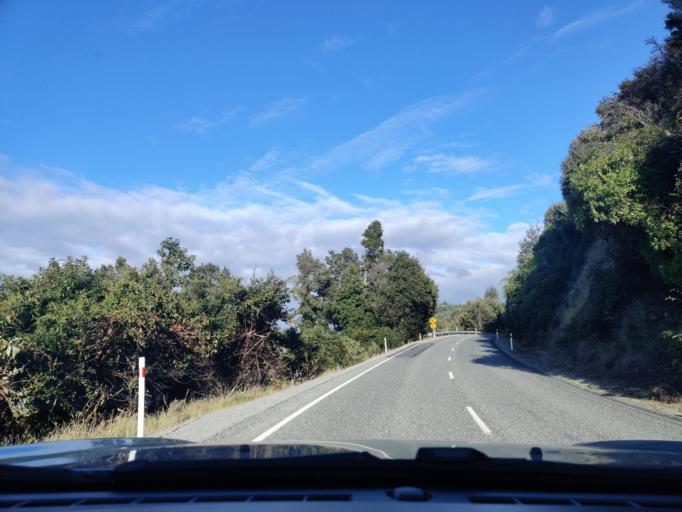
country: NZ
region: Otago
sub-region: Queenstown-Lakes District
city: Queenstown
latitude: -45.0563
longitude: 168.6025
